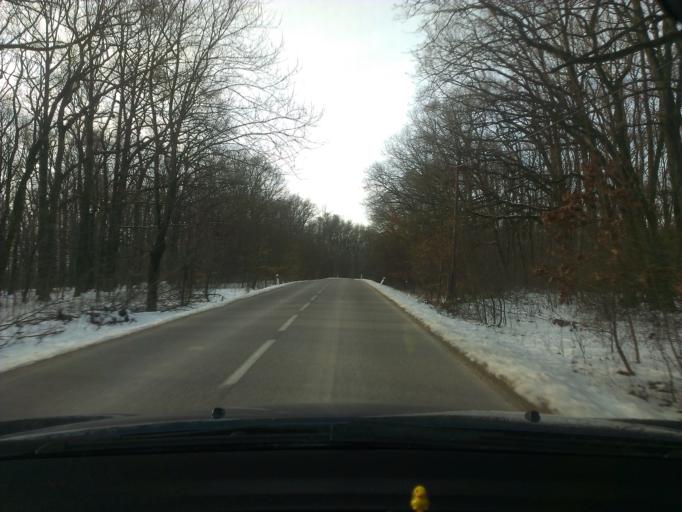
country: SK
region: Nitriansky
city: Stara Tura
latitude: 48.7253
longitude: 17.6754
